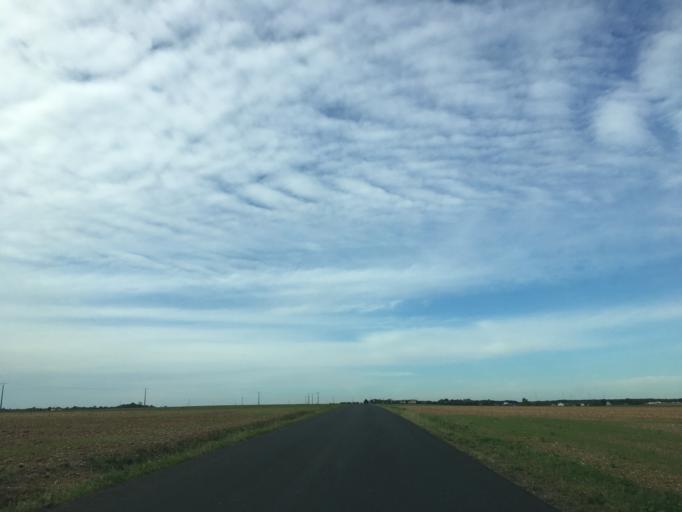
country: FR
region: Poitou-Charentes
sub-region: Departement des Deux-Sevres
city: Beauvoir-sur-Niort
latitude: 46.0709
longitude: -0.4882
